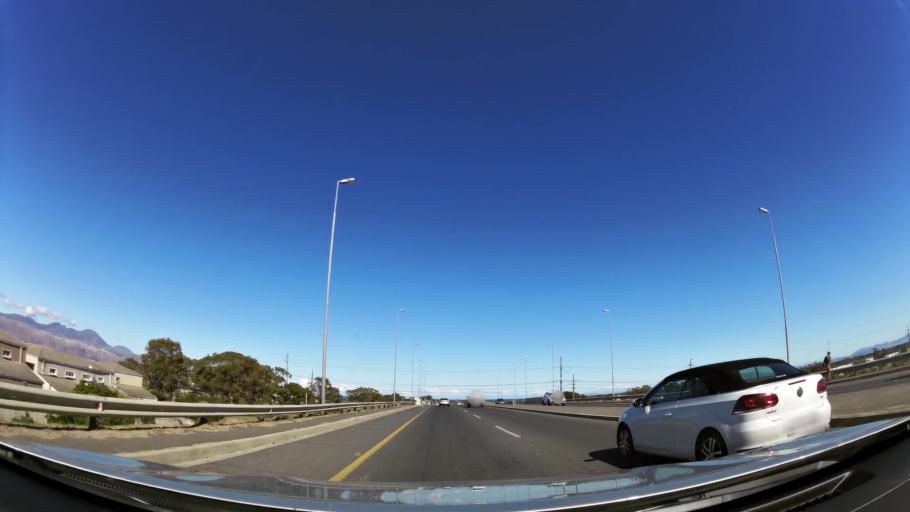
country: ZA
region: Western Cape
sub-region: Cape Winelands District Municipality
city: Stellenbosch
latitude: -34.0739
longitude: 18.8231
